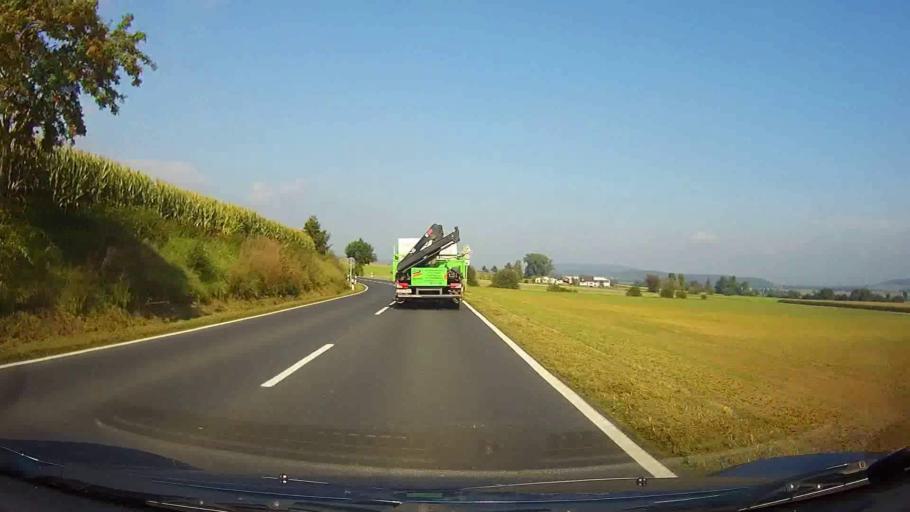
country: DE
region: Lower Saxony
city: Hardegsen
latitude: 51.6685
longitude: 9.8476
